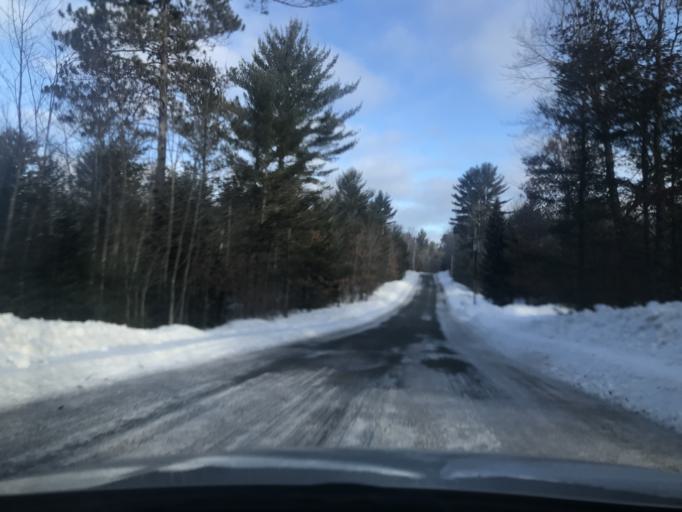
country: US
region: Wisconsin
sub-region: Marinette County
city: Niagara
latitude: 45.6294
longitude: -87.9678
